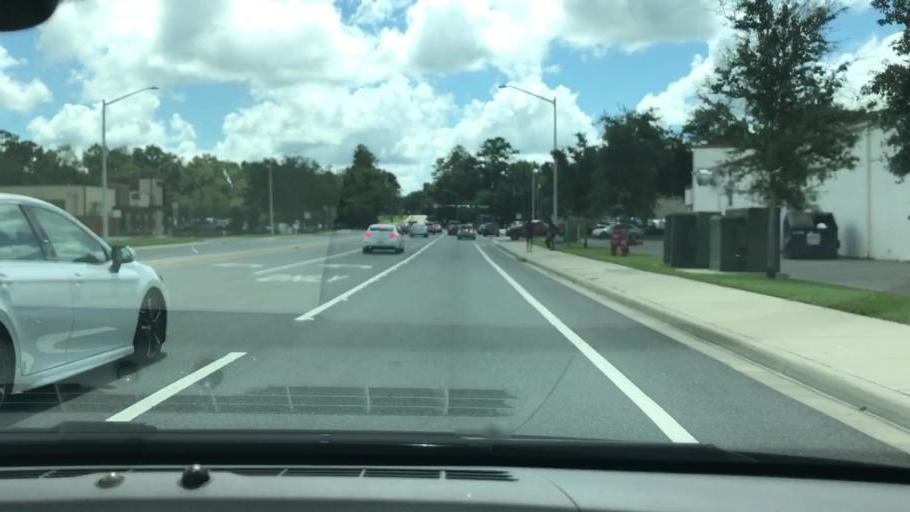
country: US
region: Florida
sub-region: Alachua County
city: Gainesville
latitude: 29.6218
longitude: -82.3812
